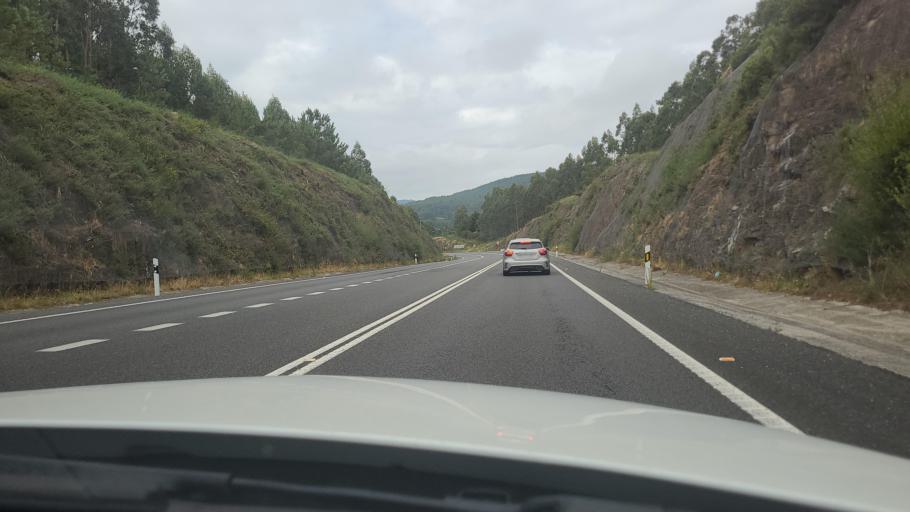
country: ES
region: Galicia
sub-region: Provincia da Coruna
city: Corcubion
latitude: 42.9476
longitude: -9.2214
